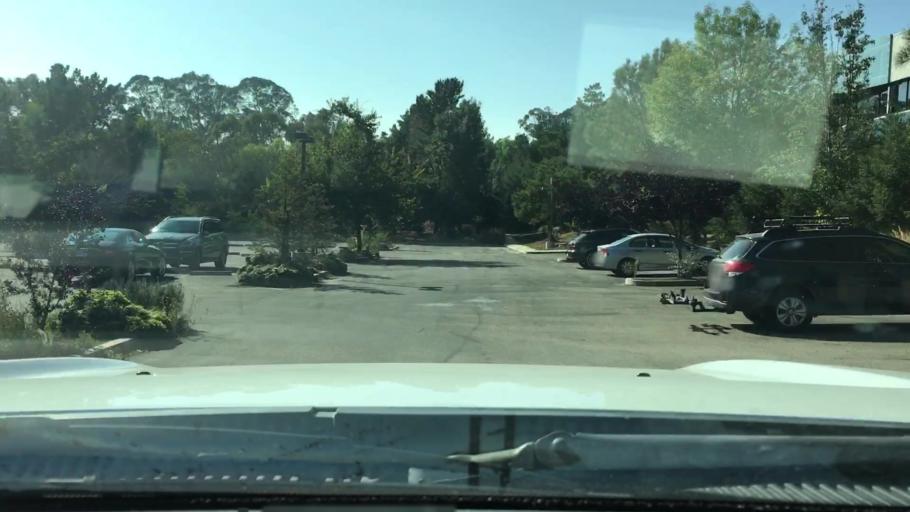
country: US
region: California
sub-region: San Luis Obispo County
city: San Luis Obispo
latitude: 35.2629
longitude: -120.6443
